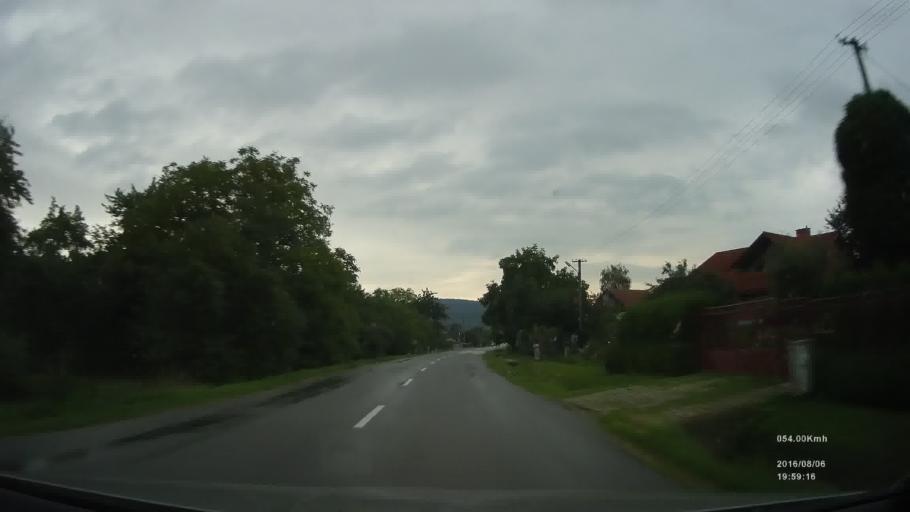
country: SK
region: Presovsky
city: Svidnik
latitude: 49.2637
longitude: 21.5801
